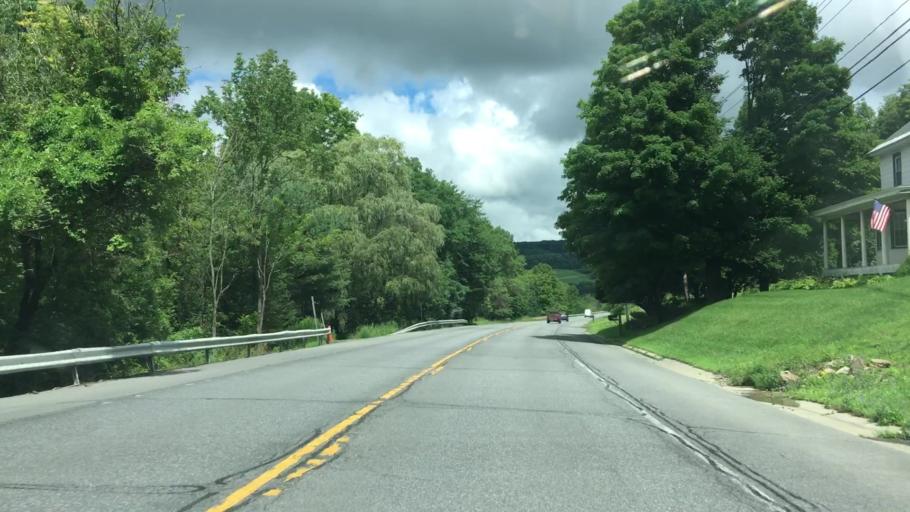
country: US
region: New York
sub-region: Rensselaer County
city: Poestenkill
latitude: 42.7943
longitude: -73.5692
